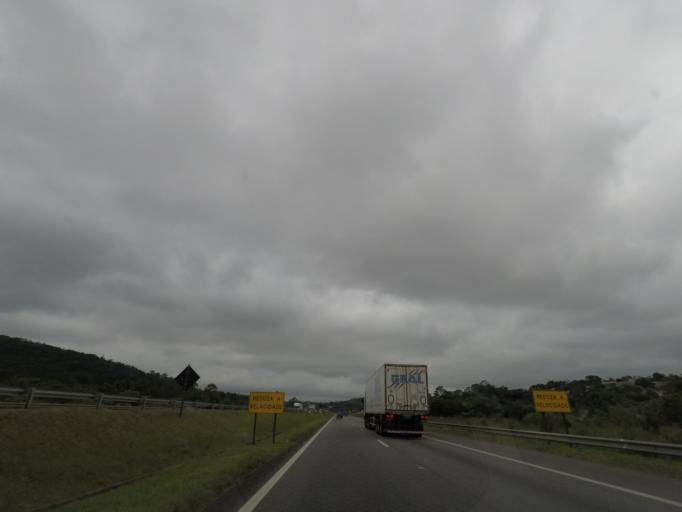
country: BR
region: Sao Paulo
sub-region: Bom Jesus Dos Perdoes
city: Bom Jesus dos Perdoes
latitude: -23.1703
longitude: -46.4380
